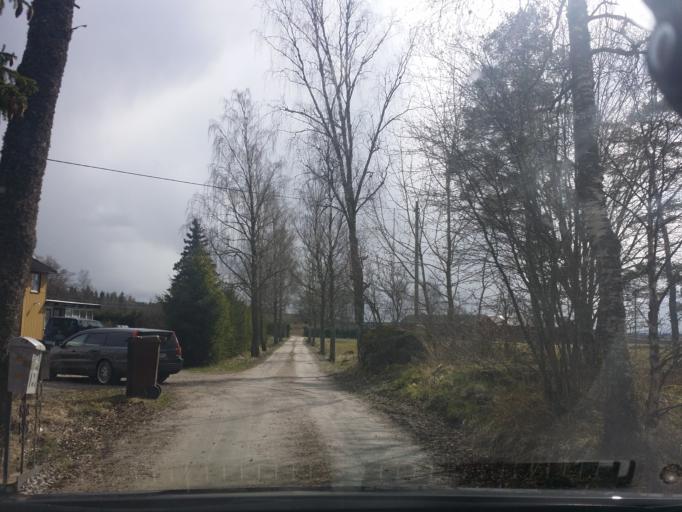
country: SE
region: Vaestmanland
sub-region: Sala Kommun
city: Sala
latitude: 59.9177
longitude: 16.6489
